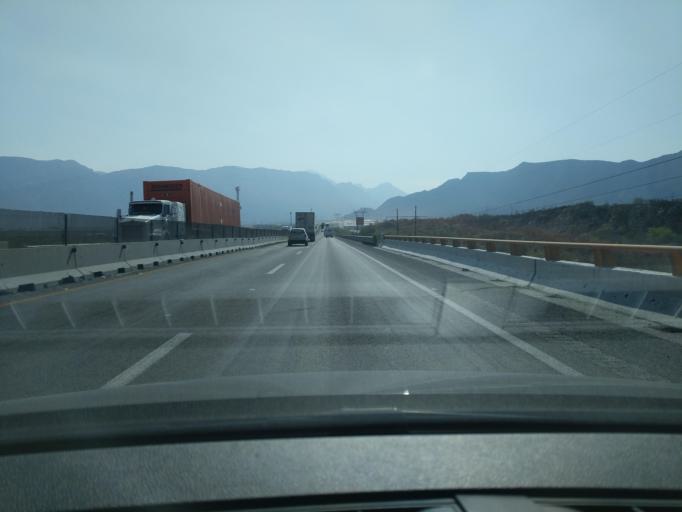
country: MX
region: Nuevo Leon
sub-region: Garcia
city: Los Parques
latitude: 25.7417
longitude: -100.5157
